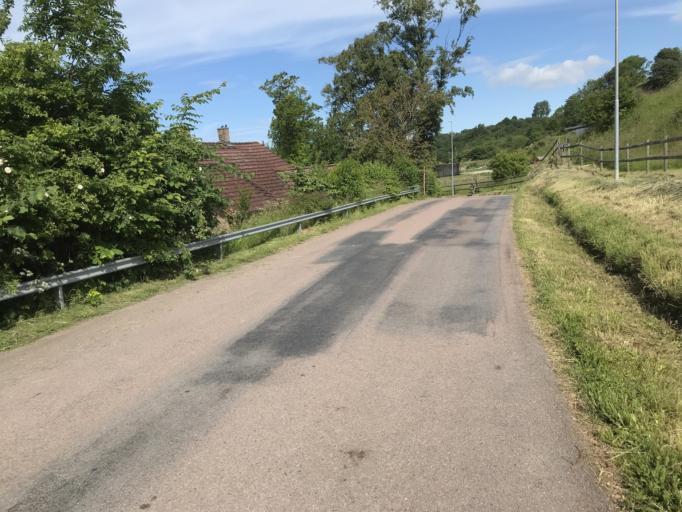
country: SE
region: Skane
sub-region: Helsingborg
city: Glumslov
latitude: 55.9325
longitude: 12.7892
